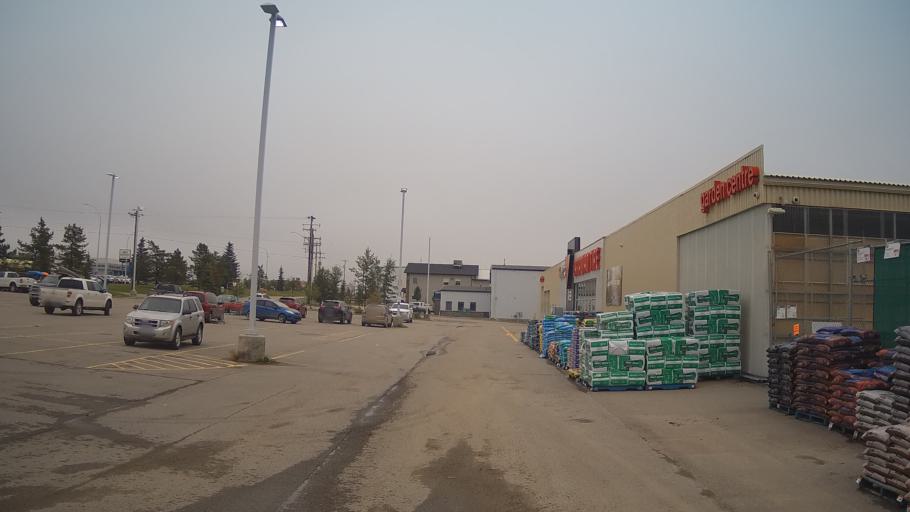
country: CA
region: Alberta
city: Edson
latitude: 53.5743
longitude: -116.4527
